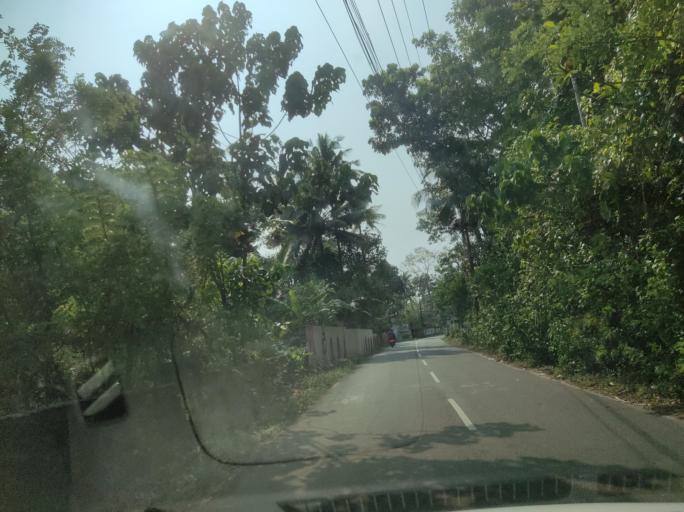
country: IN
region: Kerala
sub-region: Pattanamtitta
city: Tiruvalla
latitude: 9.3461
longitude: 76.5594
